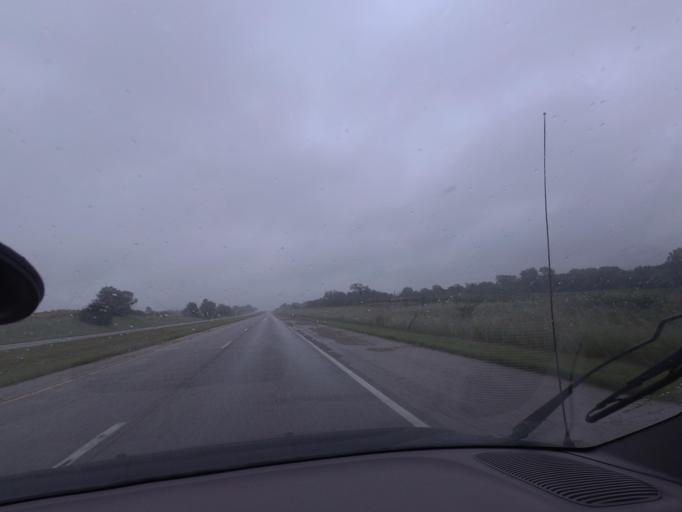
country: US
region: Illinois
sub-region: Pike County
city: Barry
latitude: 39.6889
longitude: -90.9100
